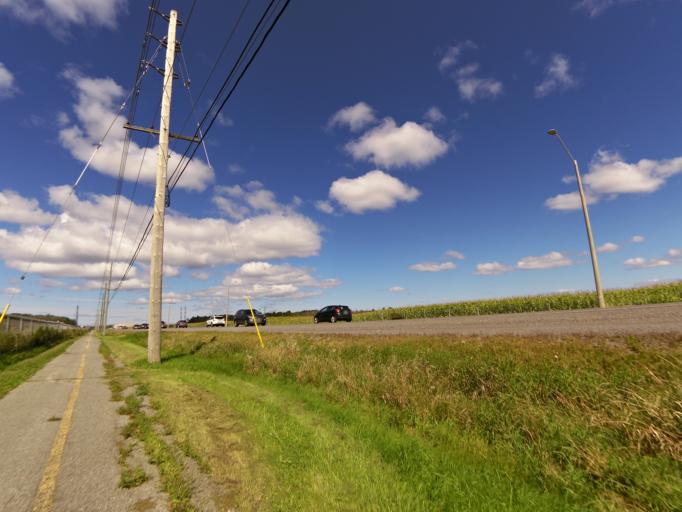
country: CA
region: Ontario
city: Bells Corners
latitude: 45.3097
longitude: -75.7700
